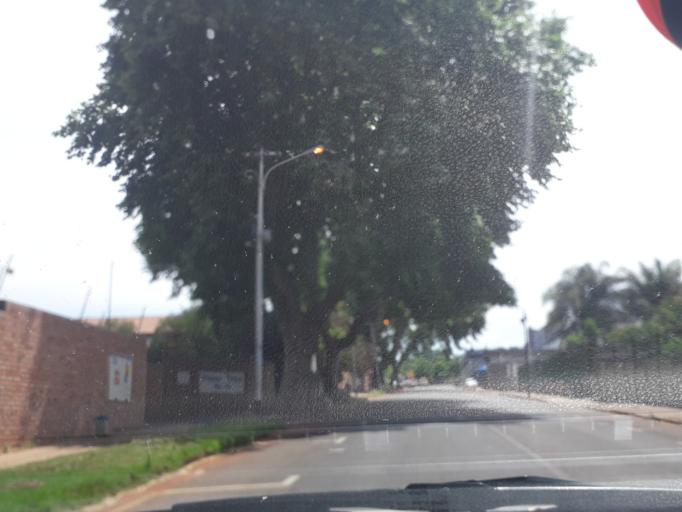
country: ZA
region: Gauteng
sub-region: City of Johannesburg Metropolitan Municipality
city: Roodepoort
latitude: -26.1767
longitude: 27.9109
